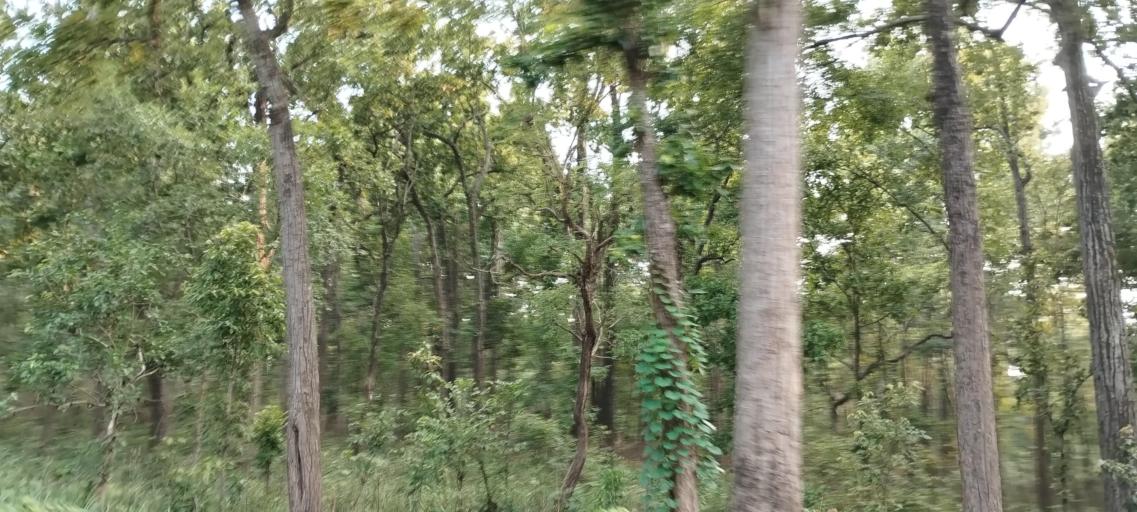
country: NP
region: Mid Western
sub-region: Bheri Zone
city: Bardiya
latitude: 28.4291
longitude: 81.3708
